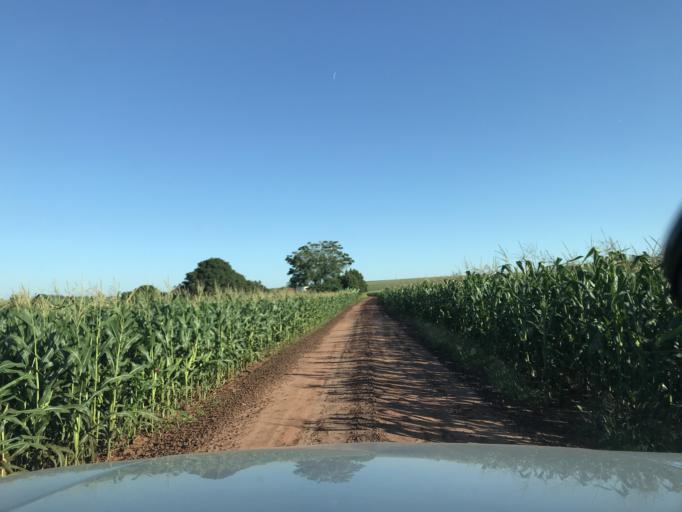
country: BR
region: Parana
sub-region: Palotina
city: Palotina
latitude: -24.2350
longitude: -53.7655
